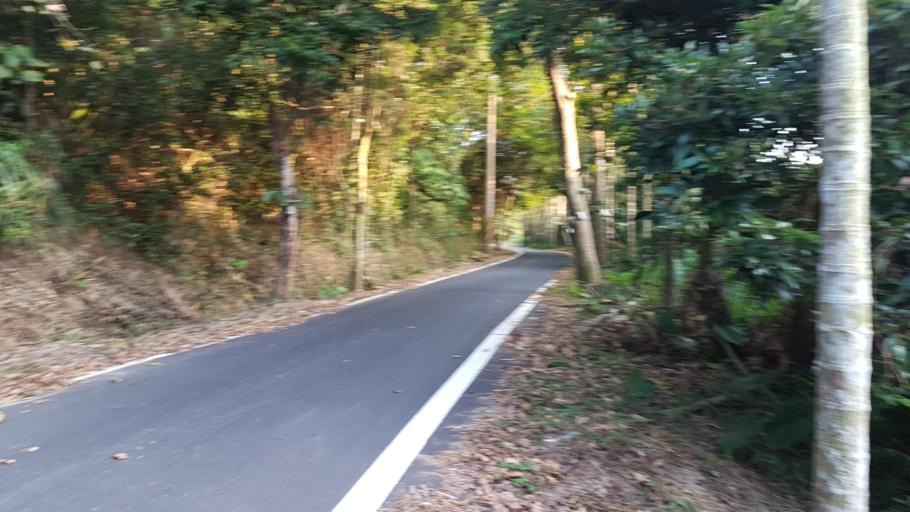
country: TW
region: Taiwan
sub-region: Chiayi
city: Jiayi Shi
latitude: 23.3629
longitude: 120.4657
